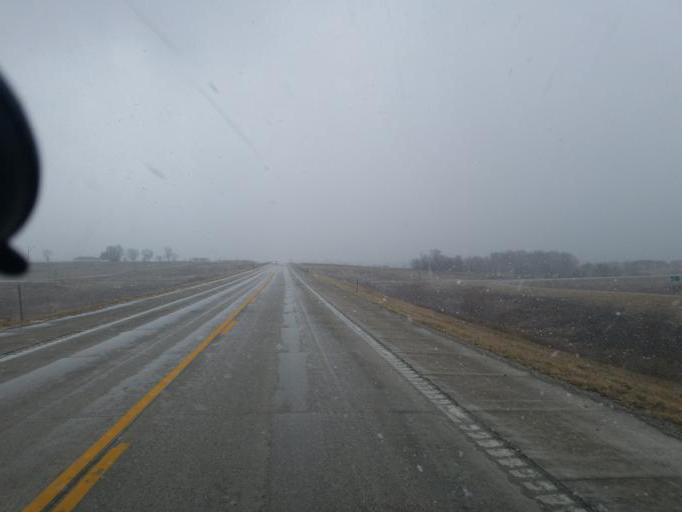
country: US
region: Missouri
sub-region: Adair County
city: Kirksville
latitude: 40.2397
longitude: -92.5795
